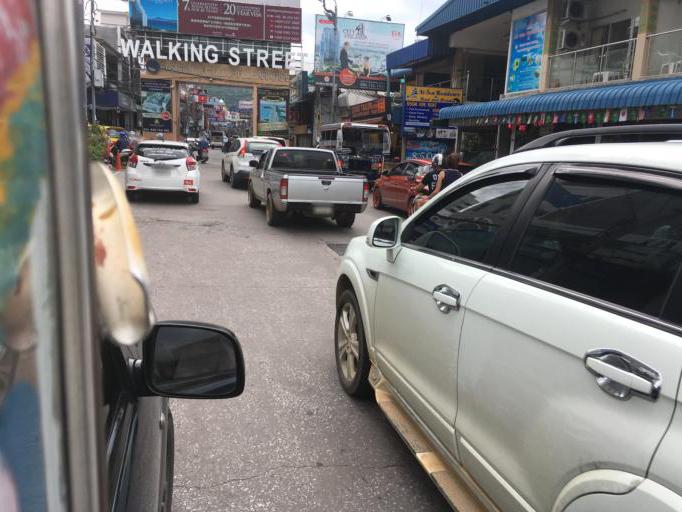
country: TH
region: Chon Buri
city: Phatthaya
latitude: 12.9276
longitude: 100.8749
